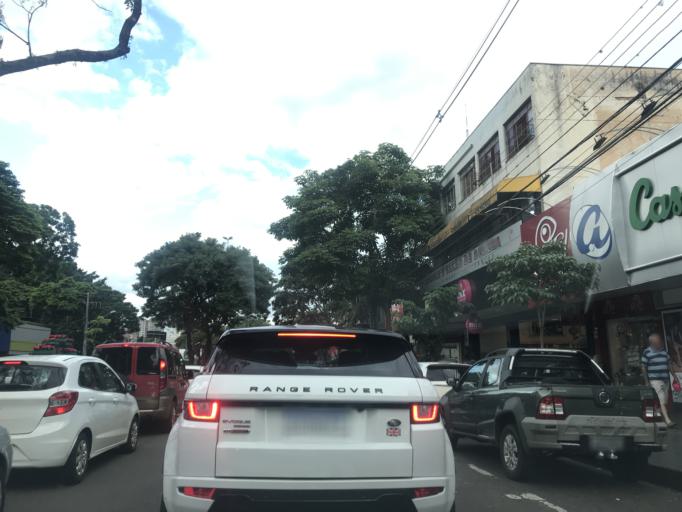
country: BR
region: Parana
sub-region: Maringa
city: Maringa
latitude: -23.4212
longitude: -51.9370
